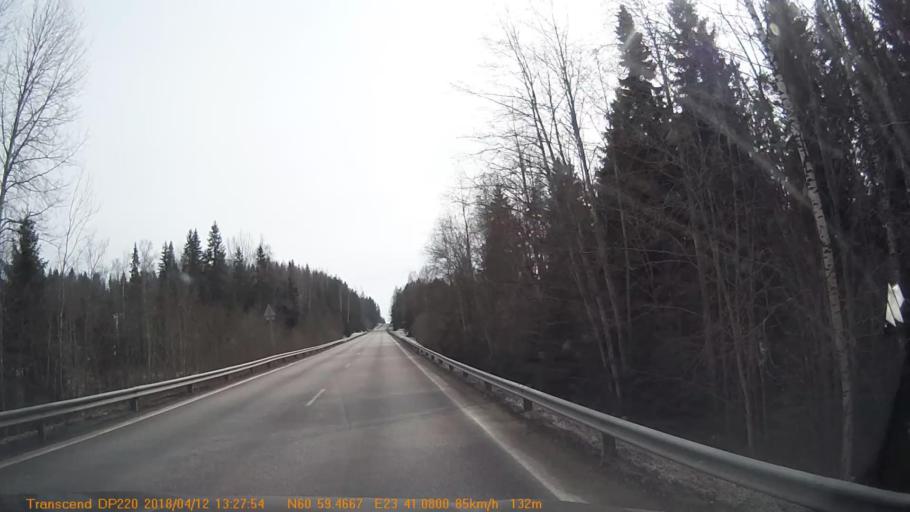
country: FI
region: Pirkanmaa
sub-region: Etelae-Pirkanmaa
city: Kylmaekoski
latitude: 60.9910
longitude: 23.6848
